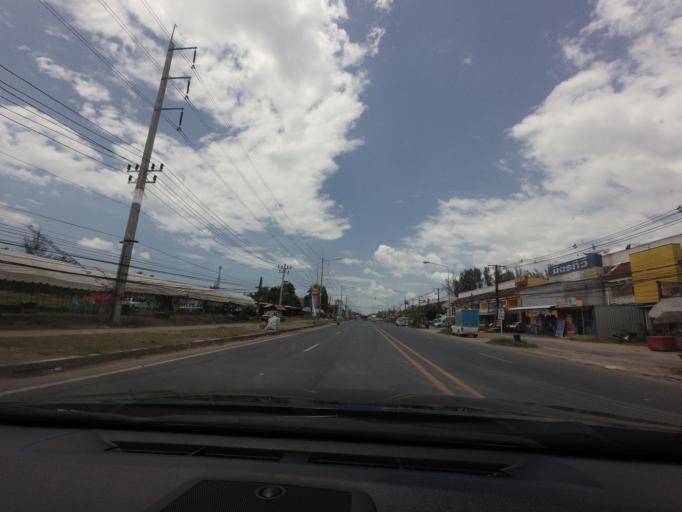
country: TH
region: Phangnga
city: Ban Khao Lak
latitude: 8.6632
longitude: 98.2532
